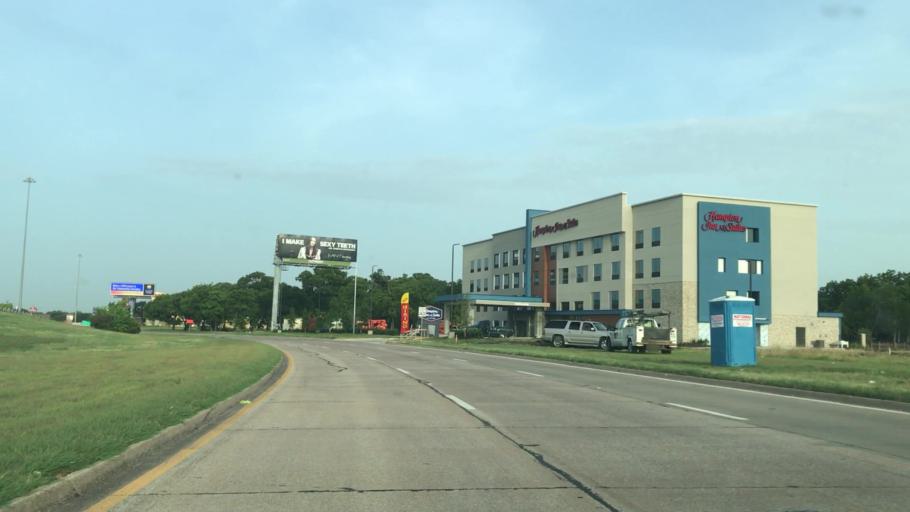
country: US
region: Texas
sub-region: Dallas County
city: Balch Springs
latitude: 32.7958
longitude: -96.6947
